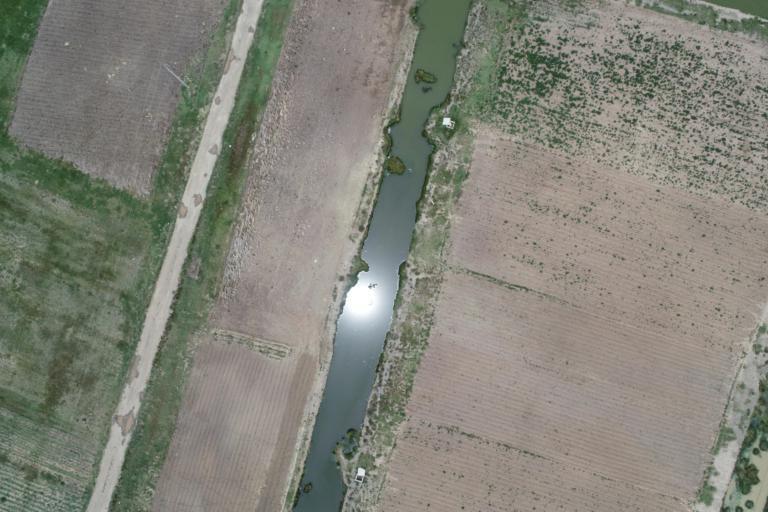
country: BO
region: La Paz
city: La Paz
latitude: -16.5182
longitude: -68.3011
